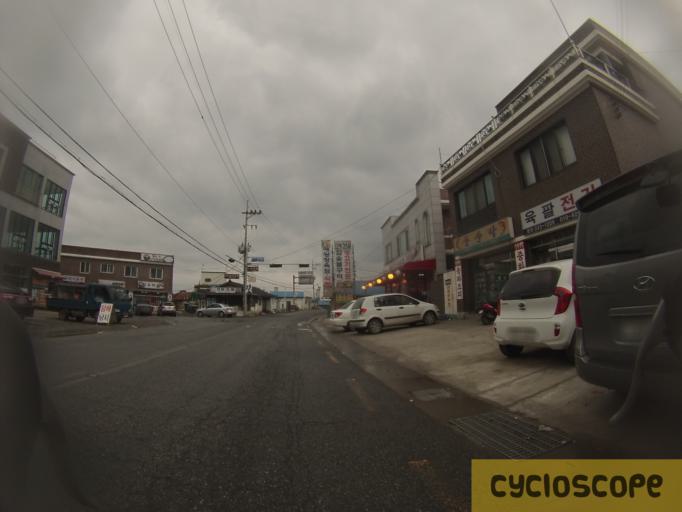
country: KR
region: Chungcheongnam-do
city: Yesan
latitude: 36.6374
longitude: 126.8006
